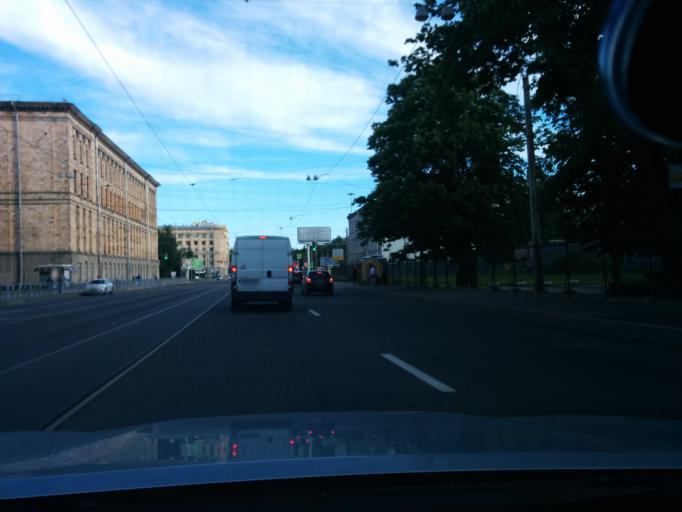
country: RU
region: Leningrad
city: Svetlanovskiy
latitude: 60.0054
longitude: 30.3268
